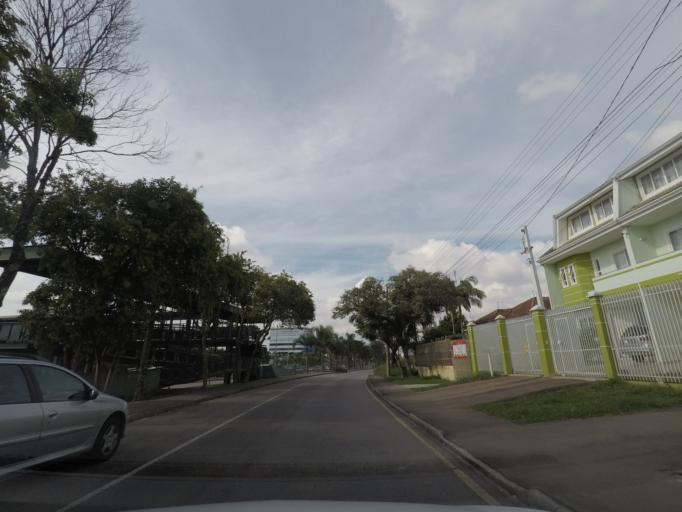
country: BR
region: Parana
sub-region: Curitiba
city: Curitiba
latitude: -25.4547
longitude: -49.2469
